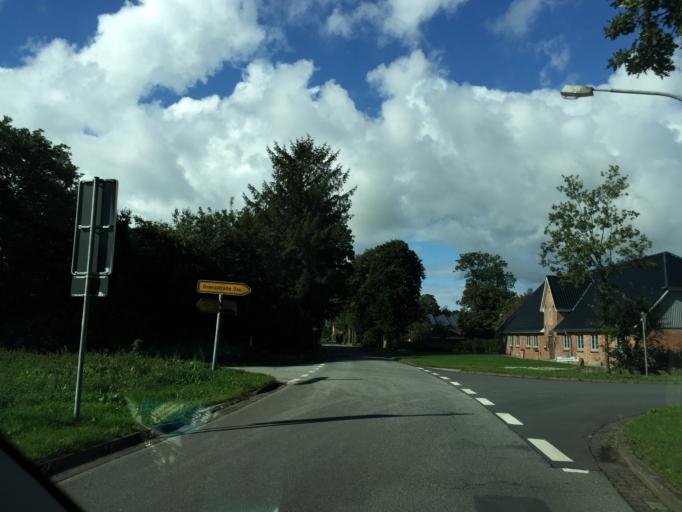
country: DE
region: Schleswig-Holstein
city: Bramstedtlund
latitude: 54.8401
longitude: 9.0876
